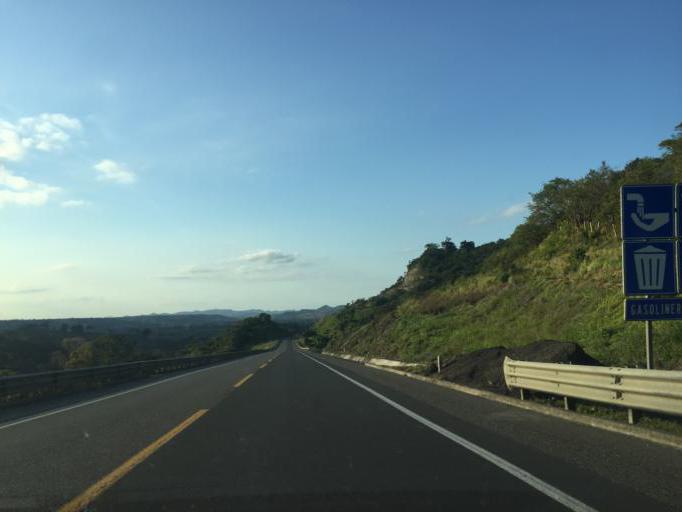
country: MX
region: Veracruz
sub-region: Papantla
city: Residencial Tajin
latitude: 20.6053
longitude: -97.3834
